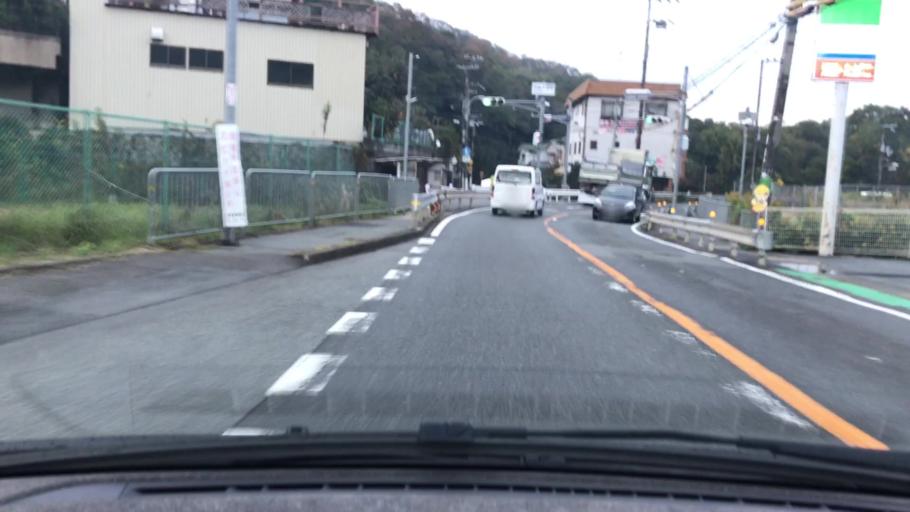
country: JP
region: Hyogo
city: Sandacho
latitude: 34.8337
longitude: 135.2839
